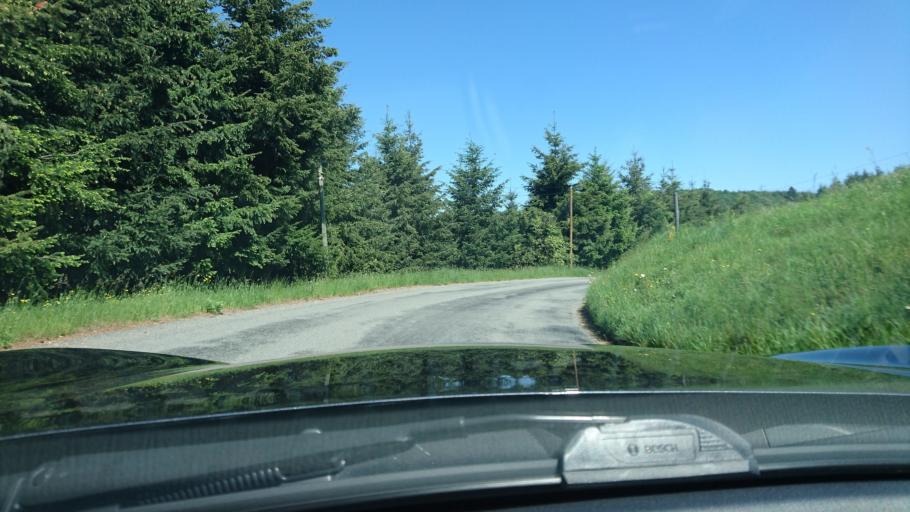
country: FR
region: Rhone-Alpes
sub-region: Departement de la Loire
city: Violay
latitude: 45.8673
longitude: 4.3451
